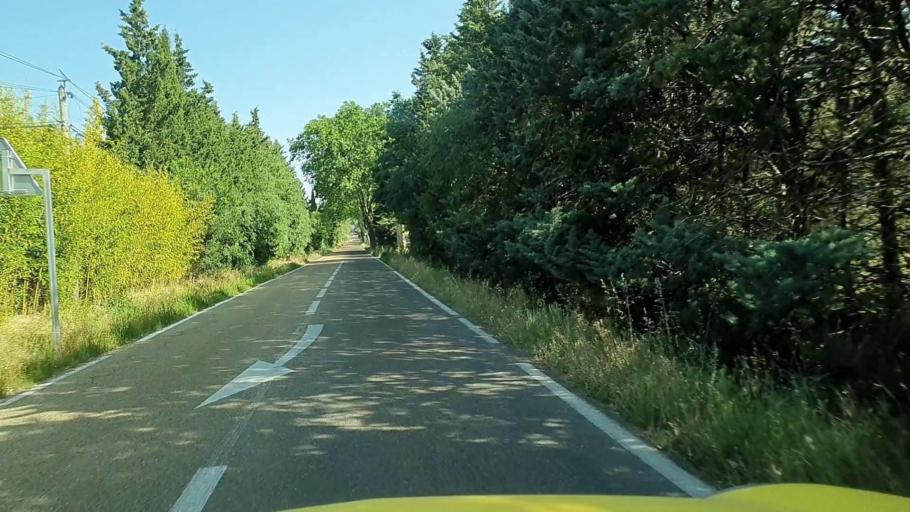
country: FR
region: Languedoc-Roussillon
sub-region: Departement du Gard
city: Montaren-et-Saint-Mediers
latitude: 44.0469
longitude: 4.4047
